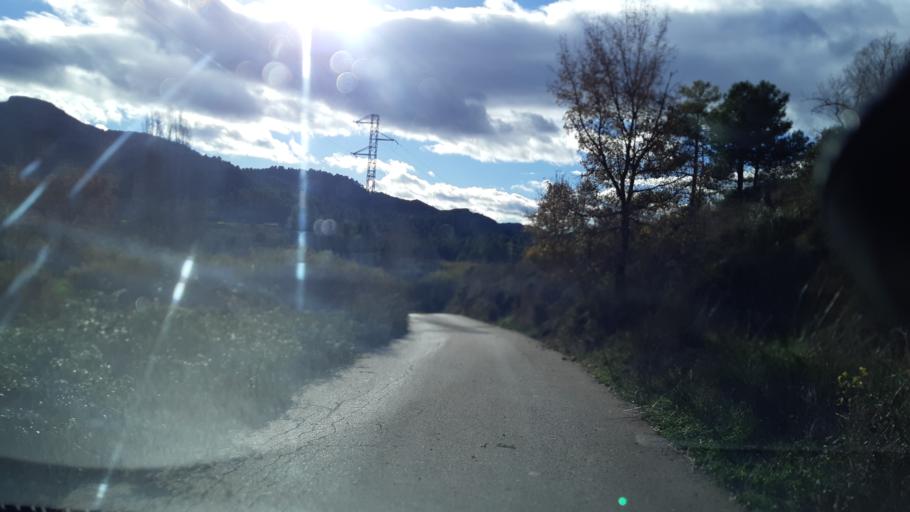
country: ES
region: Aragon
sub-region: Provincia de Teruel
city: Valderrobres
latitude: 40.8456
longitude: 0.2069
